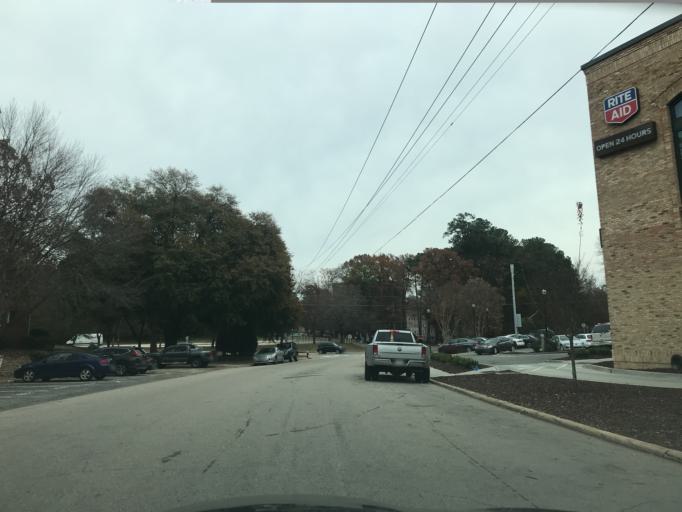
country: US
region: North Carolina
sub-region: Wake County
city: West Raleigh
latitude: 35.7918
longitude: -78.6581
